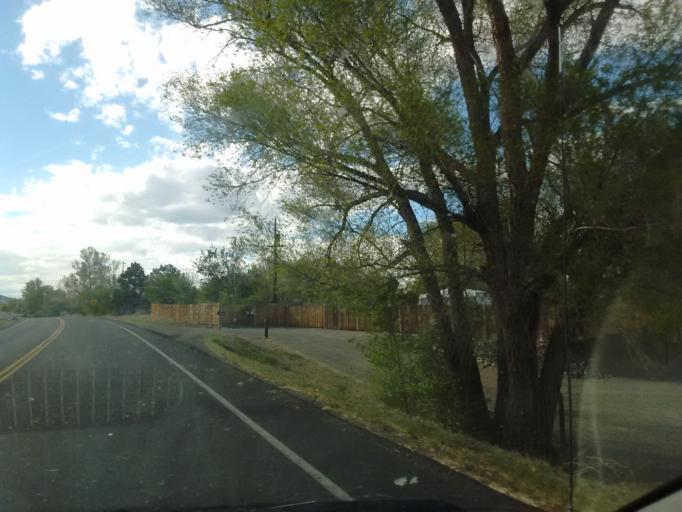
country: US
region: Colorado
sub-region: Mesa County
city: Redlands
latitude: 39.0736
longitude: -108.6226
